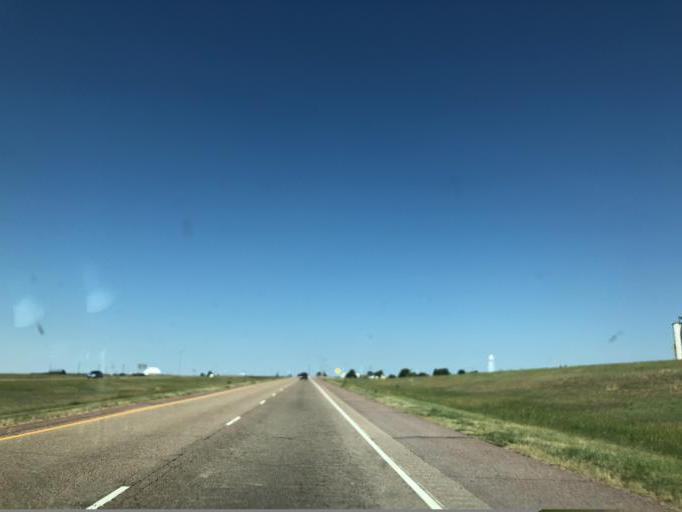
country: US
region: Colorado
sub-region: Lincoln County
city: Hugo
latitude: 39.2751
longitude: -103.4922
